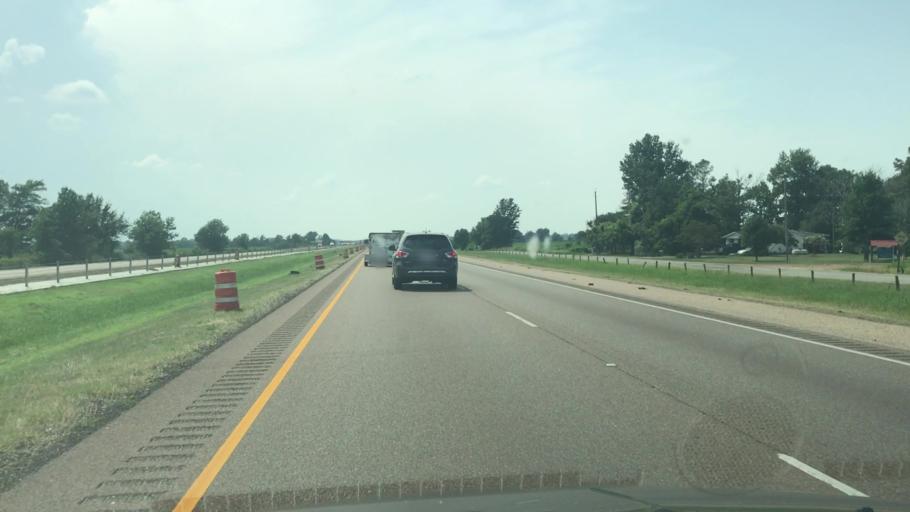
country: US
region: Arkansas
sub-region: Crittenden County
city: Earle
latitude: 35.1507
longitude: -90.3796
